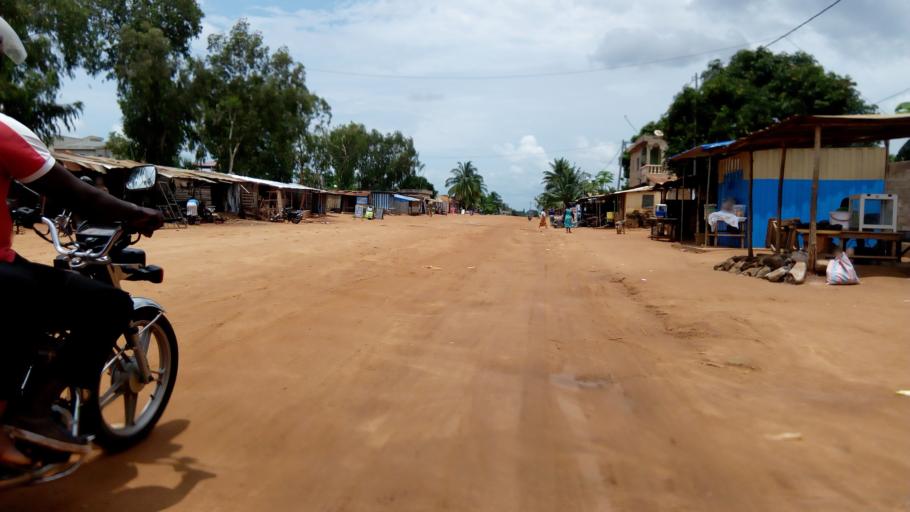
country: TG
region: Maritime
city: Lome
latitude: 6.2263
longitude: 1.1601
